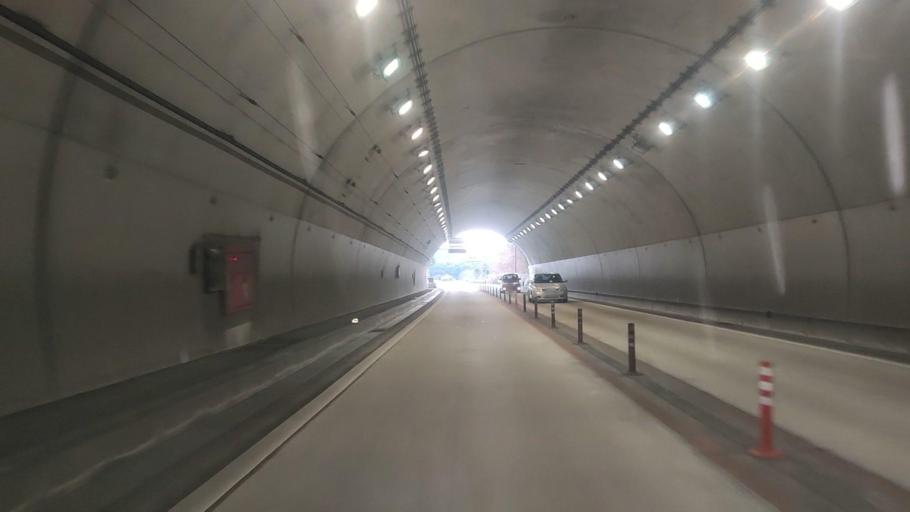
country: JP
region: Nagasaki
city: Shimabara
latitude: 32.7714
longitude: 130.3575
